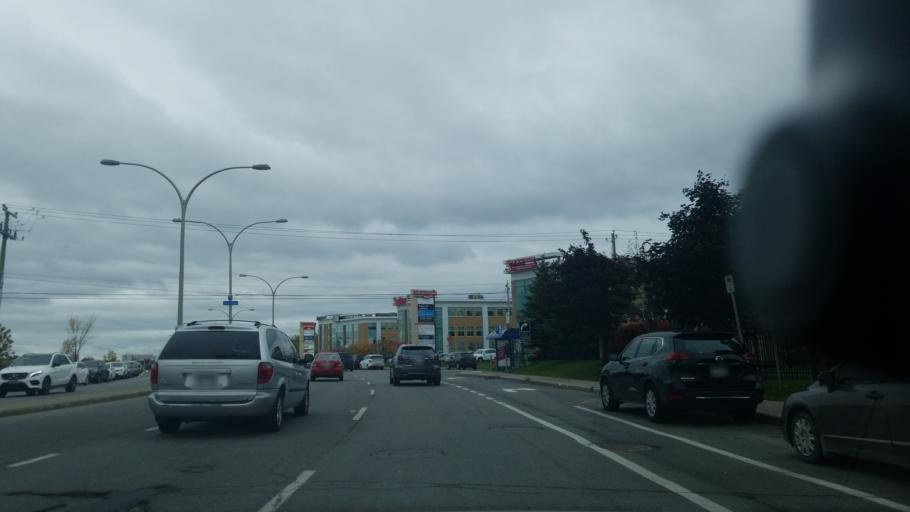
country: CA
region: Quebec
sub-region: Laval
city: Laval
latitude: 45.5637
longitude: -73.7239
